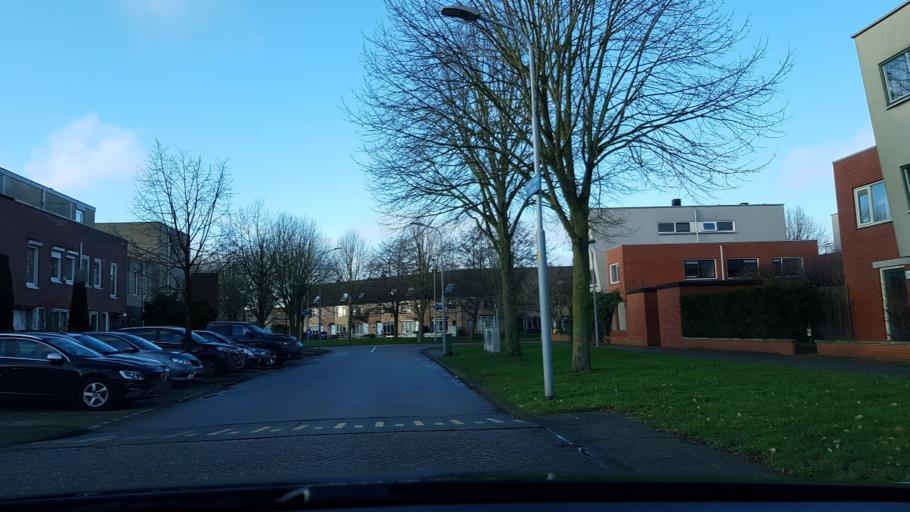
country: NL
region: North Holland
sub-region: Gemeente Haarlemmermeer
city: Hoofddorp
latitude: 52.2935
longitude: 4.6727
